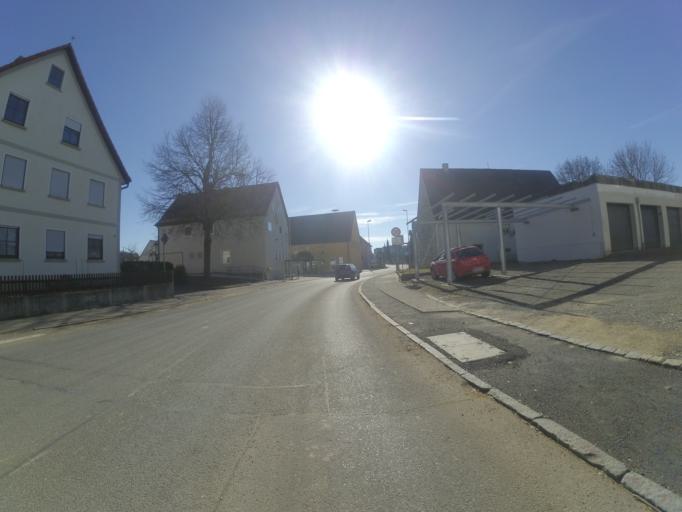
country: DE
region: Baden-Wuerttemberg
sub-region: Tuebingen Region
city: Huttisheim
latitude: 48.2797
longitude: 9.9428
